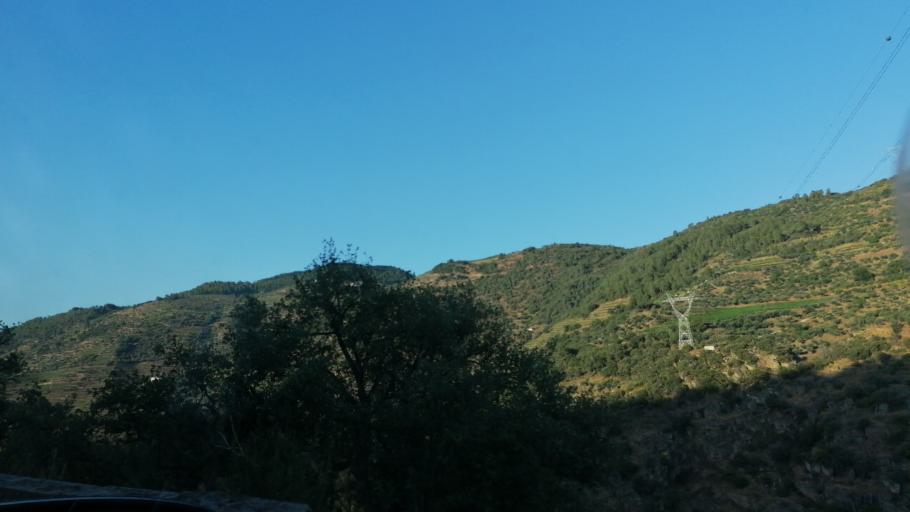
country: PT
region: Viseu
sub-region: Sao Joao da Pesqueira
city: Sao Joao da Pesqueira
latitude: 41.2217
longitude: -7.4235
